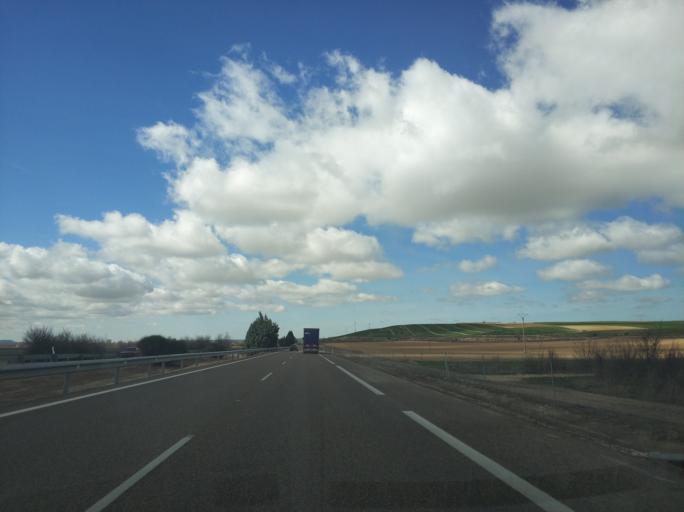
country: ES
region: Castille and Leon
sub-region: Provincia de Palencia
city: Reinoso de Cerrato
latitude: 42.0000
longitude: -4.3803
